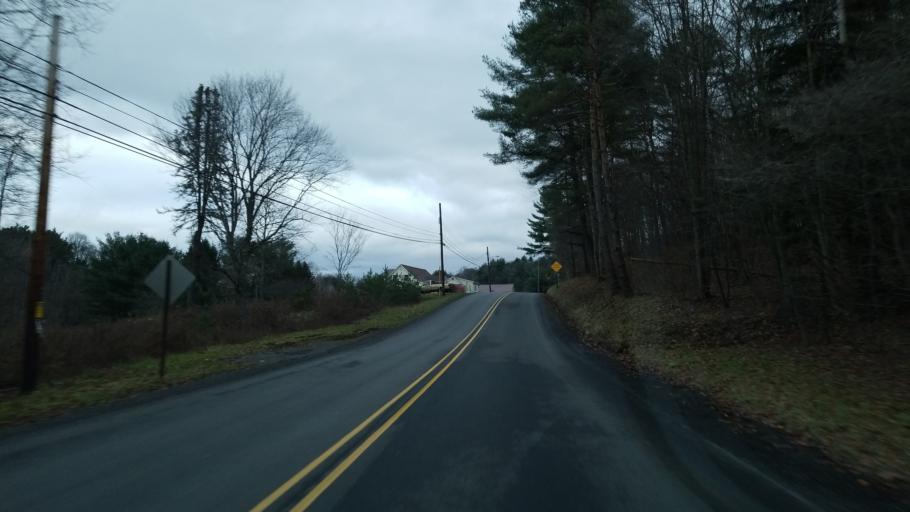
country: US
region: Pennsylvania
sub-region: Clearfield County
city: Sandy
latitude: 41.1173
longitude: -78.7941
